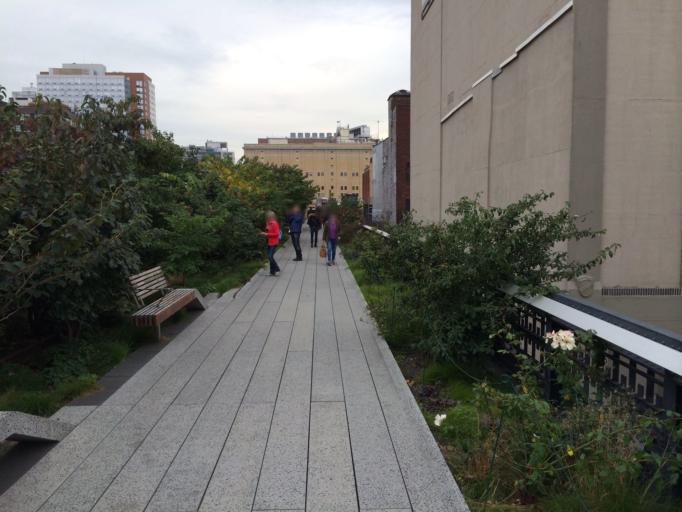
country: US
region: New Jersey
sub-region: Hudson County
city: Hoboken
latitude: 40.7467
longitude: -74.0056
